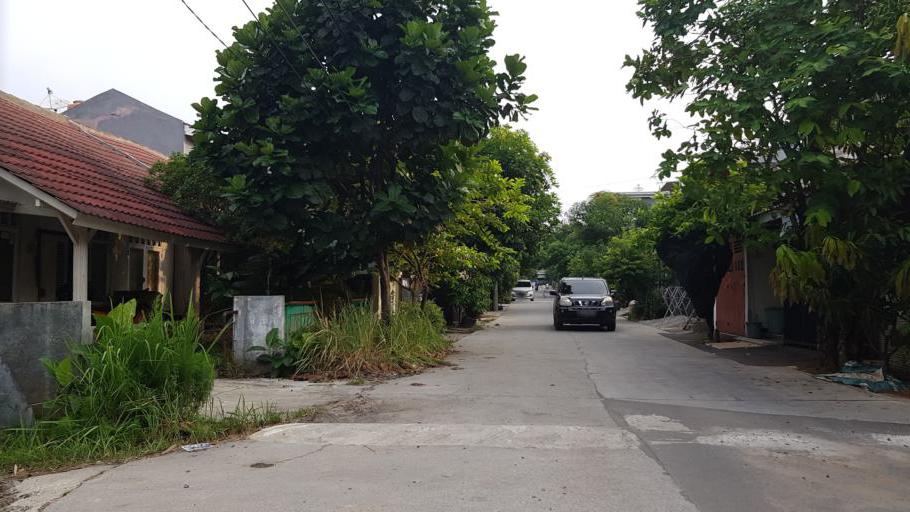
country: ID
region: West Java
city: Depok
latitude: -6.3711
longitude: 106.7953
